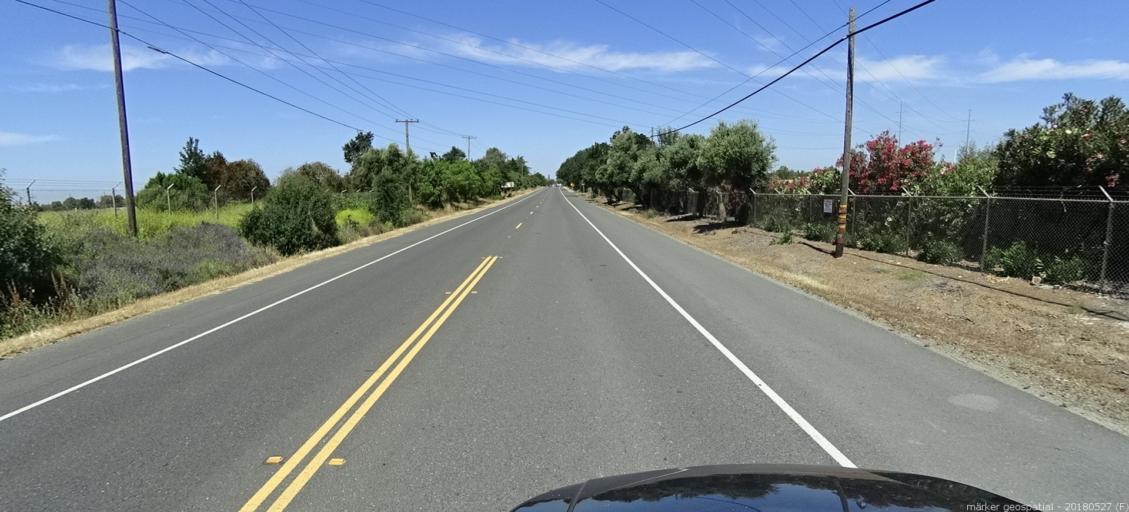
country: US
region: California
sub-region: Sacramento County
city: Rosemont
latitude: 38.5426
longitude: -121.3847
